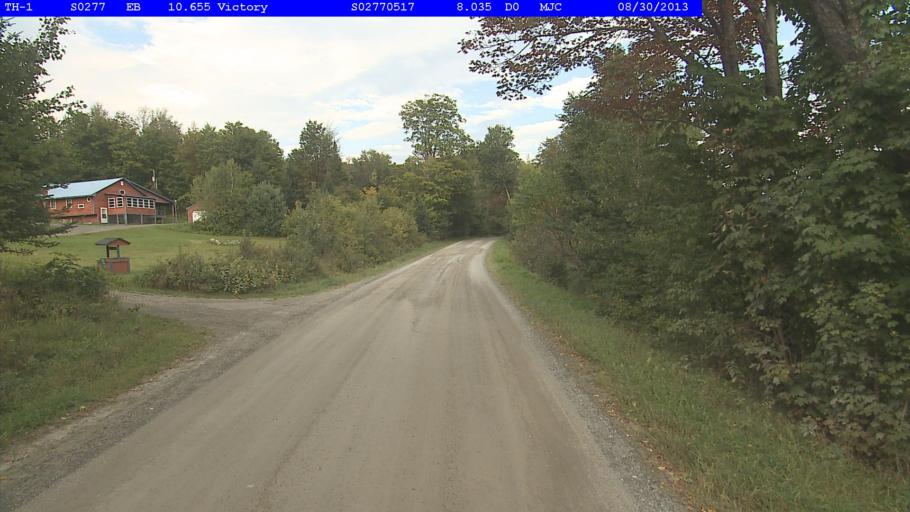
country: US
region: Vermont
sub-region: Essex County
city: Guildhall
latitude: 44.5705
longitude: -71.7745
